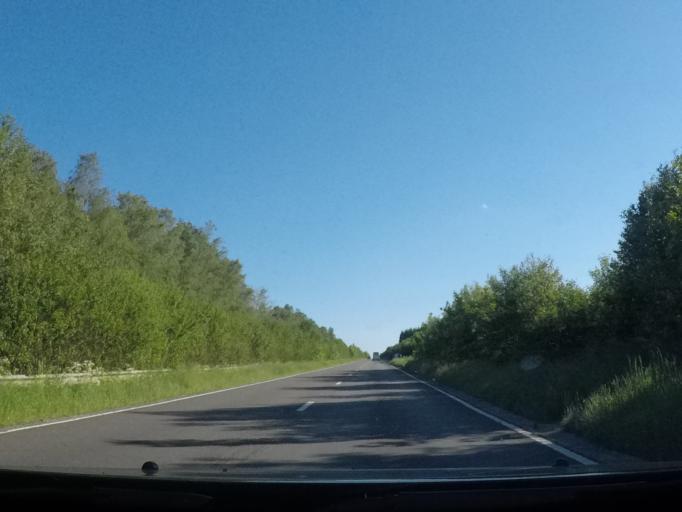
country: BE
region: Wallonia
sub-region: Province du Luxembourg
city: Saint-Hubert
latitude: 49.9879
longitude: 5.3792
